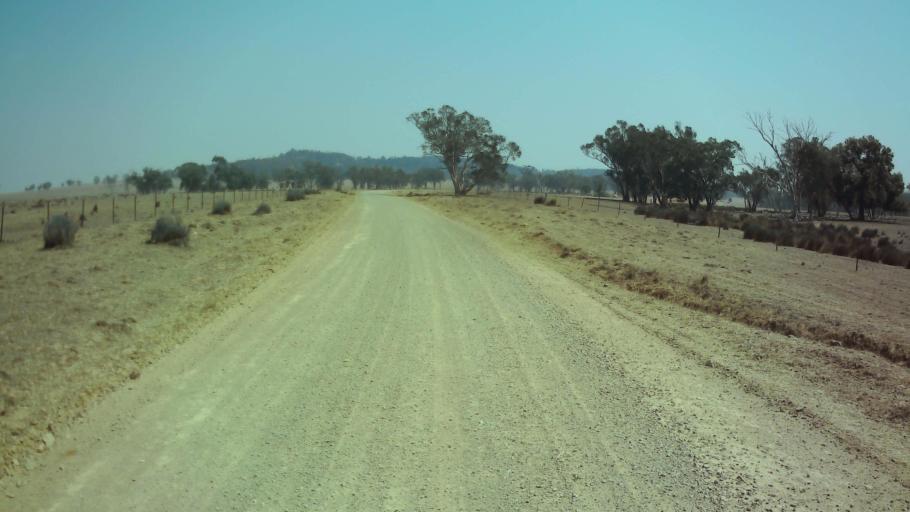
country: AU
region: New South Wales
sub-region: Weddin
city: Grenfell
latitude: -33.6776
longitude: 148.2766
